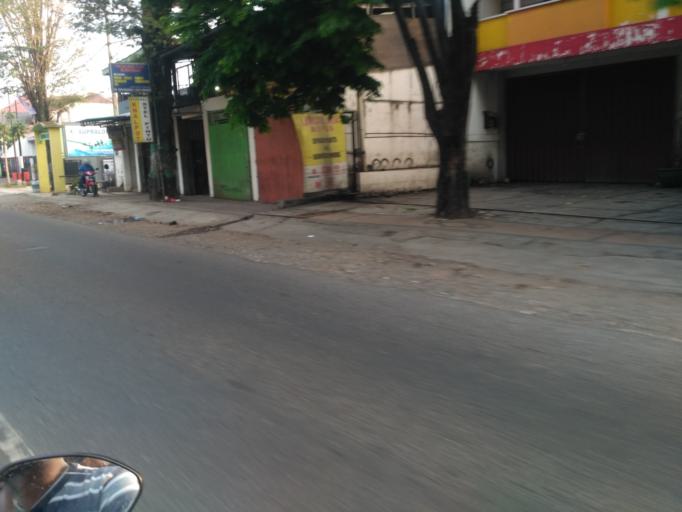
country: ID
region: East Java
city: Kepuh
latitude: -8.0116
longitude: 112.6203
